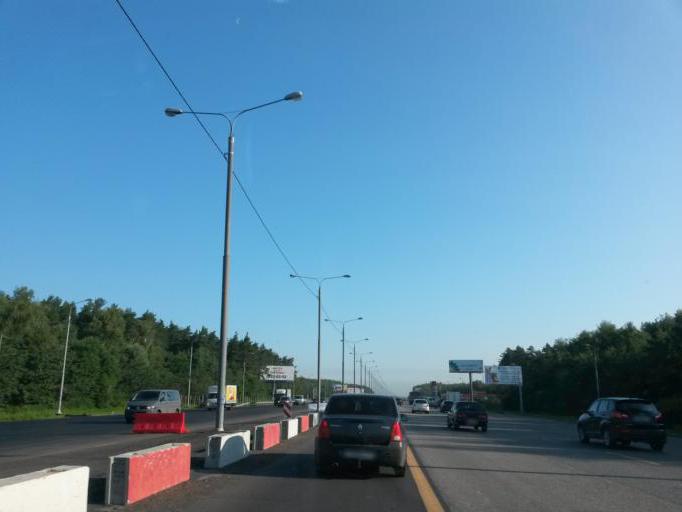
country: RU
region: Moskovskaya
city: Shcherbinka
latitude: 55.4888
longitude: 37.6125
